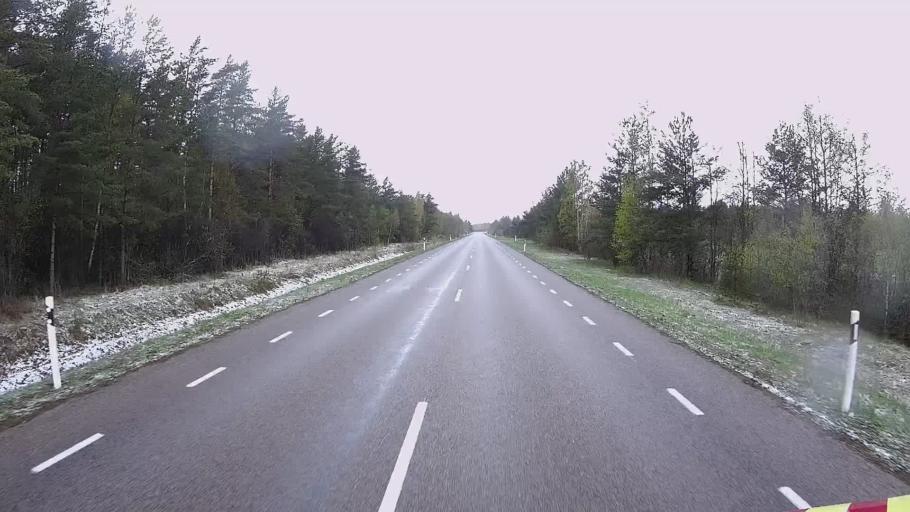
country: EE
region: Hiiumaa
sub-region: Kaerdla linn
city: Kardla
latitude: 58.7799
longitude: 22.5020
